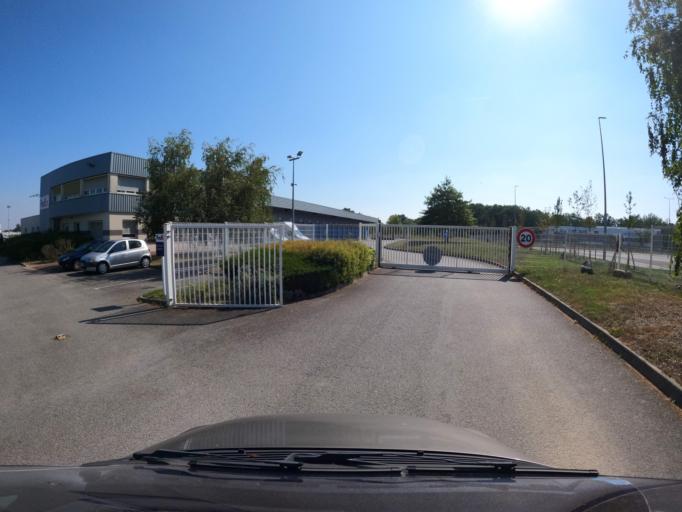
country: FR
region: Pays de la Loire
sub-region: Departement de la Loire-Atlantique
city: Pont-Saint-Martin
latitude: 47.1508
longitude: -1.6025
